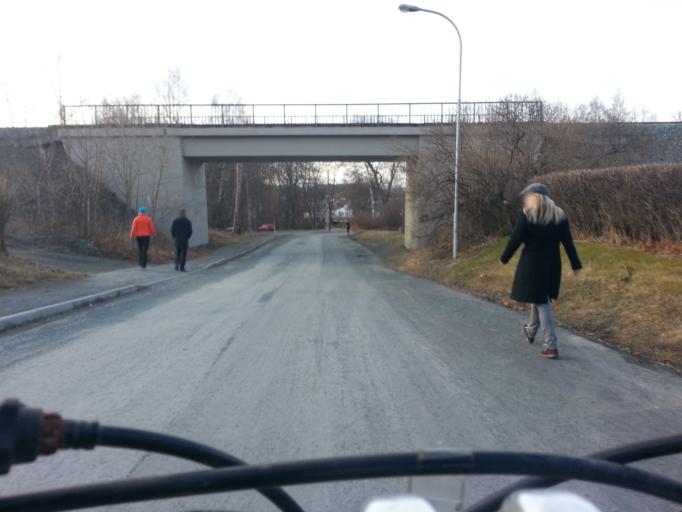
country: NO
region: Sor-Trondelag
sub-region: Trondheim
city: Trondheim
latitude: 63.4394
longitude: 10.4454
